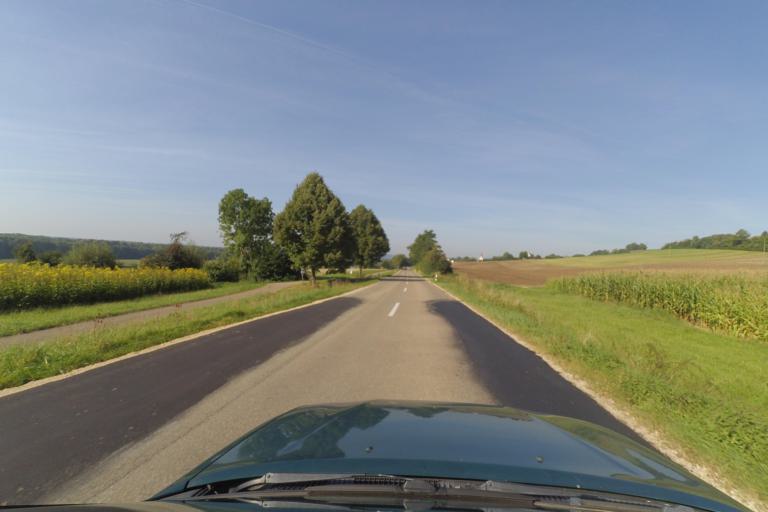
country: DE
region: Bavaria
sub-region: Swabia
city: Marxheim
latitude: 48.7425
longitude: 10.9255
